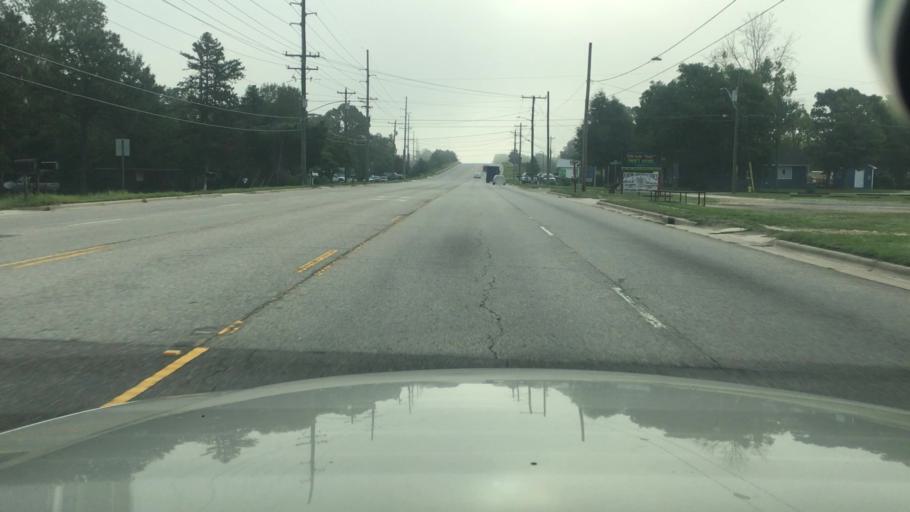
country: US
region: North Carolina
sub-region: Cumberland County
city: Hope Mills
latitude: 35.0158
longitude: -78.9288
